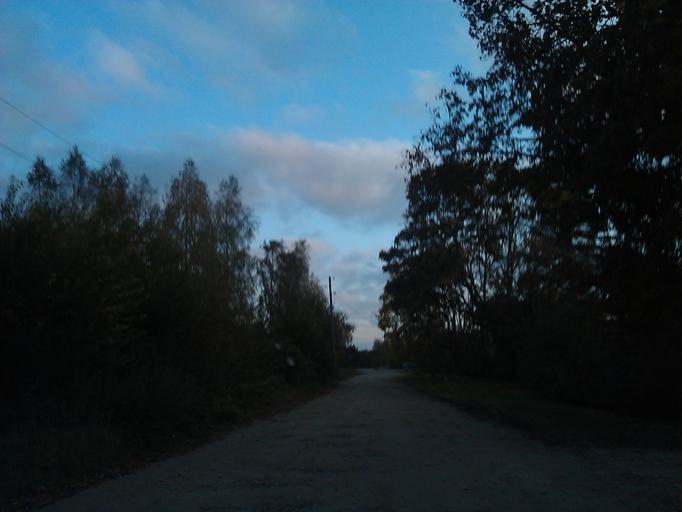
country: LV
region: Adazi
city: Adazi
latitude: 57.0702
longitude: 24.3316
